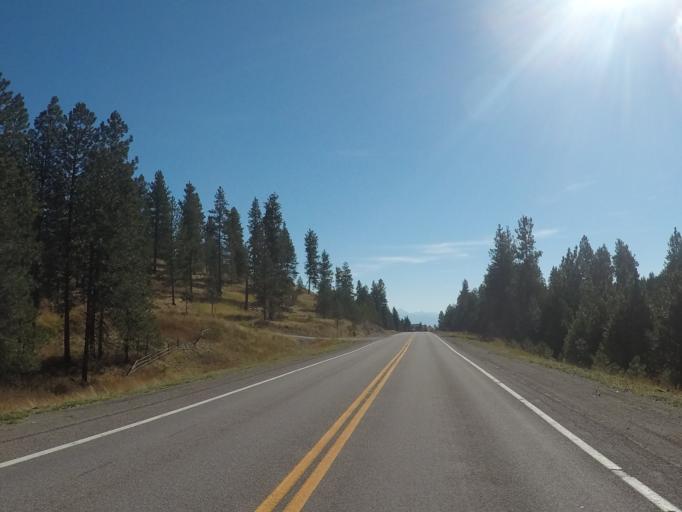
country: US
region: Montana
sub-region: Lake County
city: Polson
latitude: 47.7646
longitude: -114.2379
